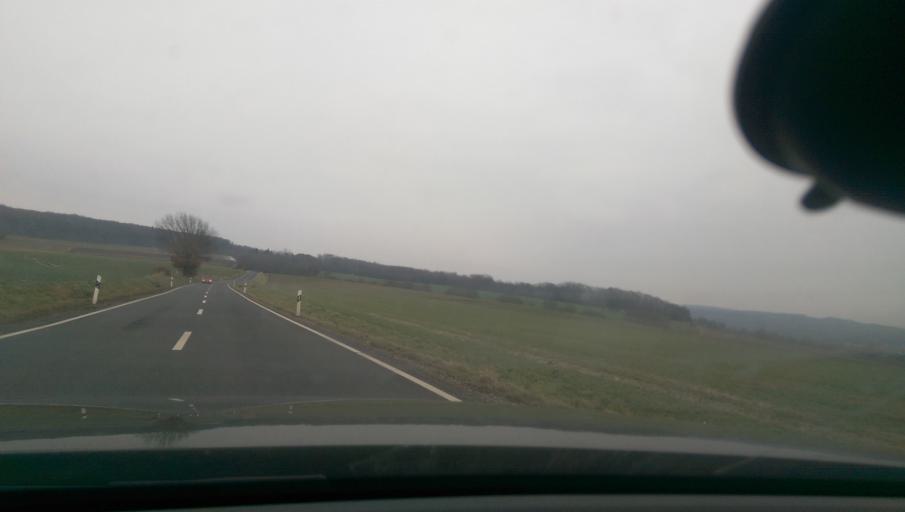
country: DE
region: Hesse
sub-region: Regierungsbezirk Kassel
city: Kaufungen
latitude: 51.3063
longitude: 9.5970
